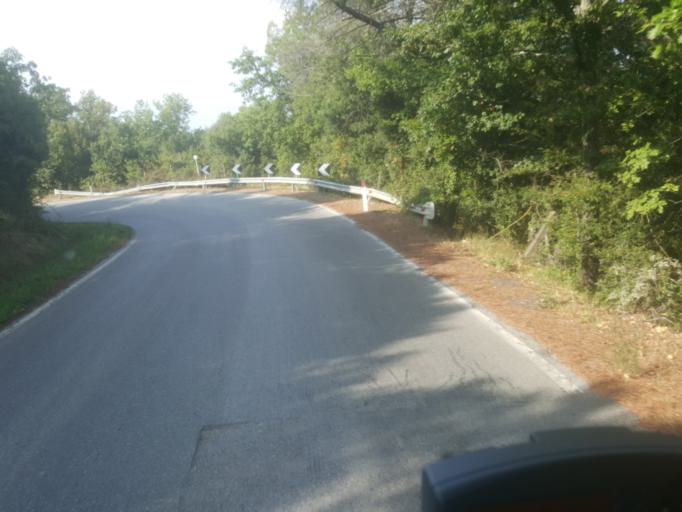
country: IT
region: Tuscany
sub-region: Province of Florence
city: Gambassi Terme
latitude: 43.5035
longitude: 10.9291
